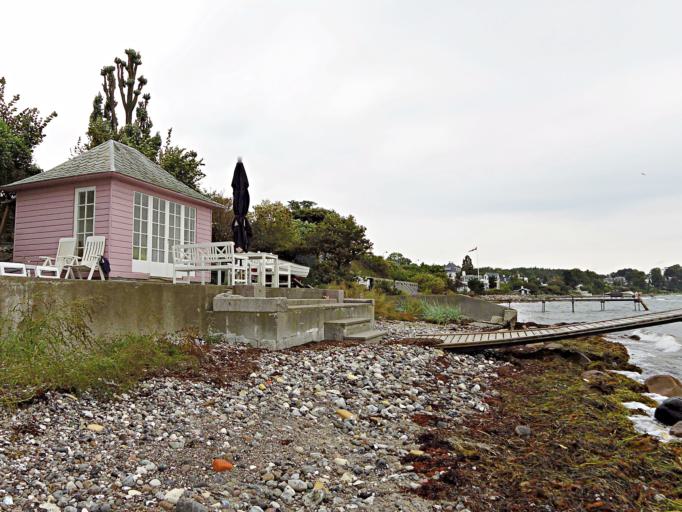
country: DK
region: Capital Region
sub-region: Rudersdal Kommune
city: Trorod
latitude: 55.8095
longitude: 12.5796
